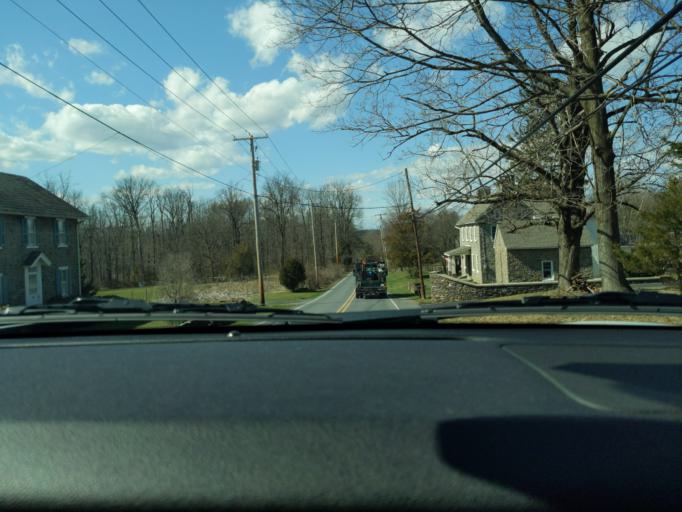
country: US
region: Pennsylvania
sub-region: Bucks County
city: Richlandtown
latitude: 40.4583
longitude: -75.2655
